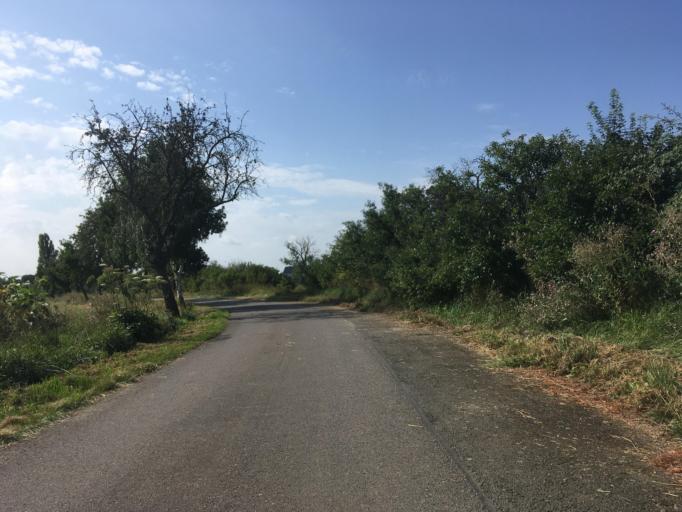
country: DE
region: Saxony
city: Elsnig
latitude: 51.6172
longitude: 12.9250
